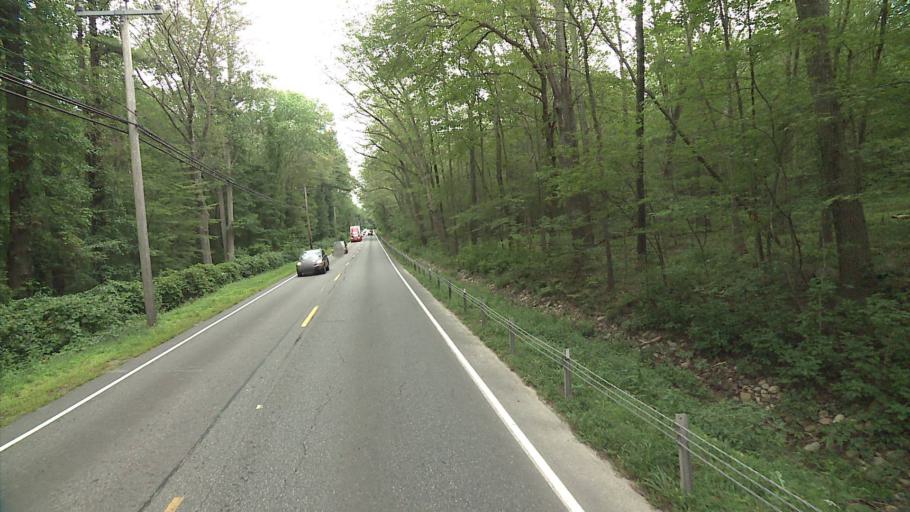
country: US
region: Connecticut
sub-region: New London County
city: Montville Center
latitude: 41.4196
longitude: -72.1968
